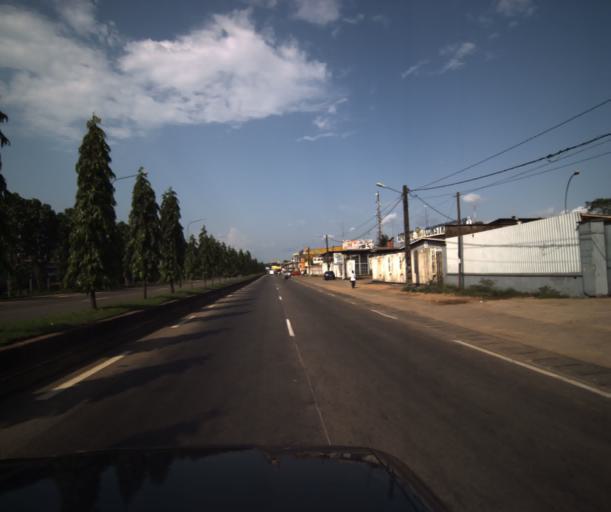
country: CM
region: Littoral
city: Douala
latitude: 4.0588
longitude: 9.6984
